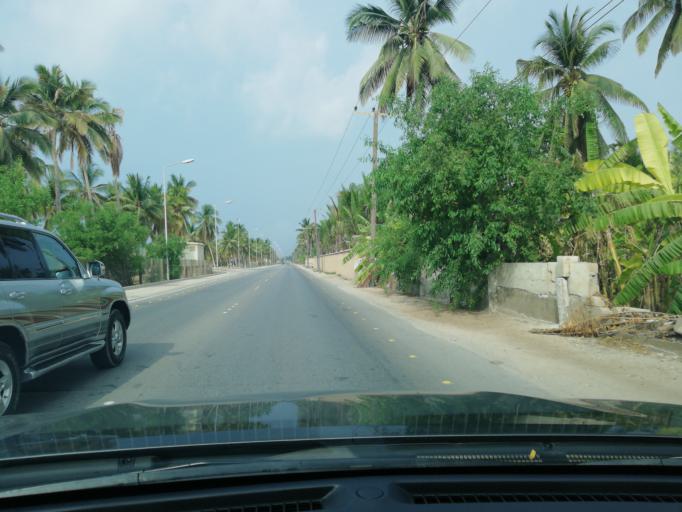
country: OM
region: Zufar
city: Salalah
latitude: 17.0117
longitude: 54.1416
